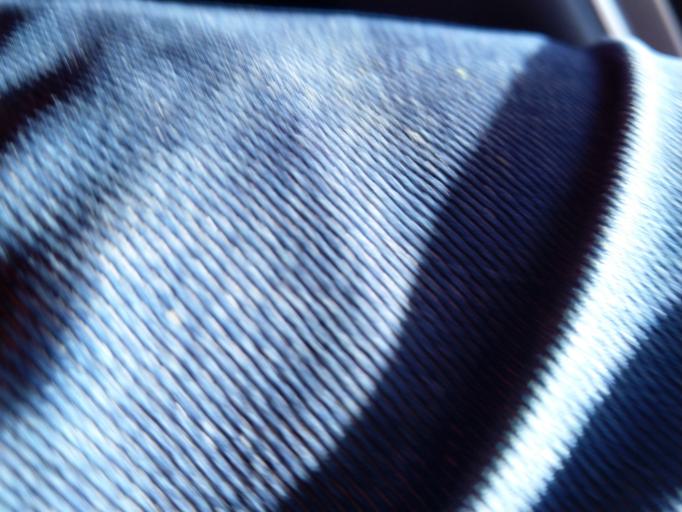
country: GB
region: Scotland
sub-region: Eilean Siar
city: Barra
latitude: 56.4851
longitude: -6.8949
